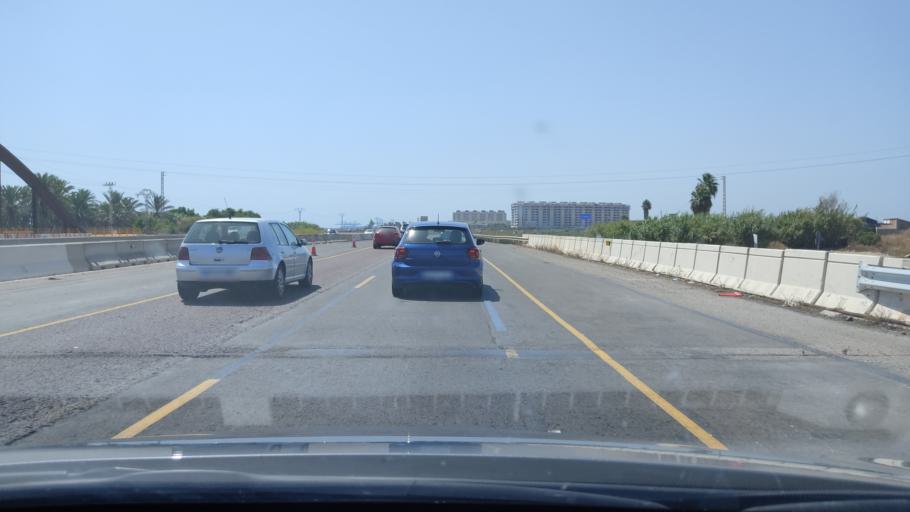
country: ES
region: Valencia
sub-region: Provincia de Valencia
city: Alboraya
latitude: 39.5028
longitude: -0.3261
